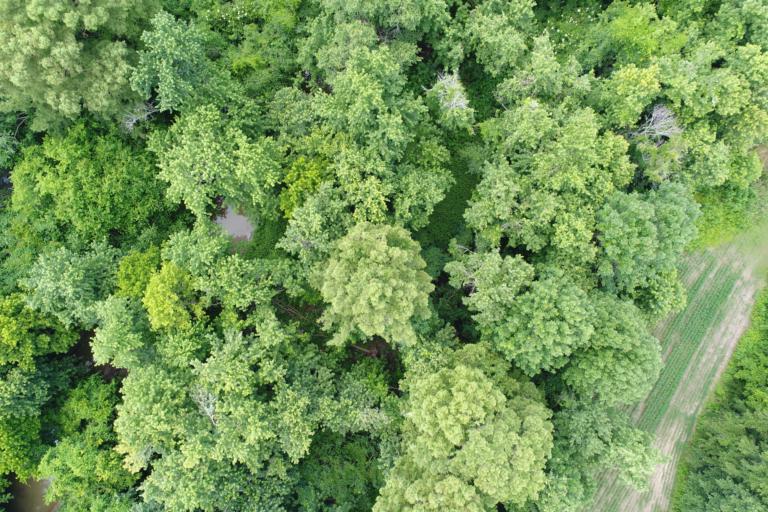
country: US
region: Mississippi
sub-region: De Soto County
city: Walls
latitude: 34.9136
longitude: -90.2051
